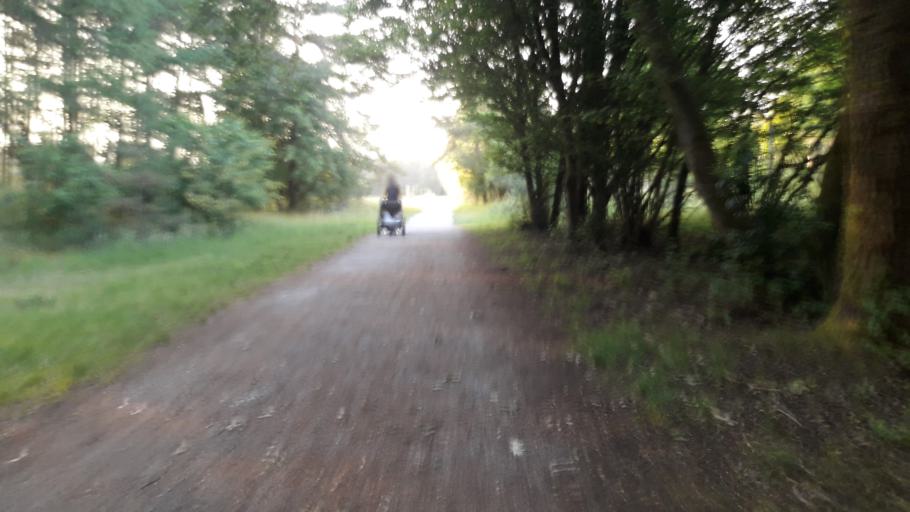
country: DE
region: North Rhine-Westphalia
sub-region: Regierungsbezirk Detmold
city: Augustdorf
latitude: 51.8618
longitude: 8.6961
